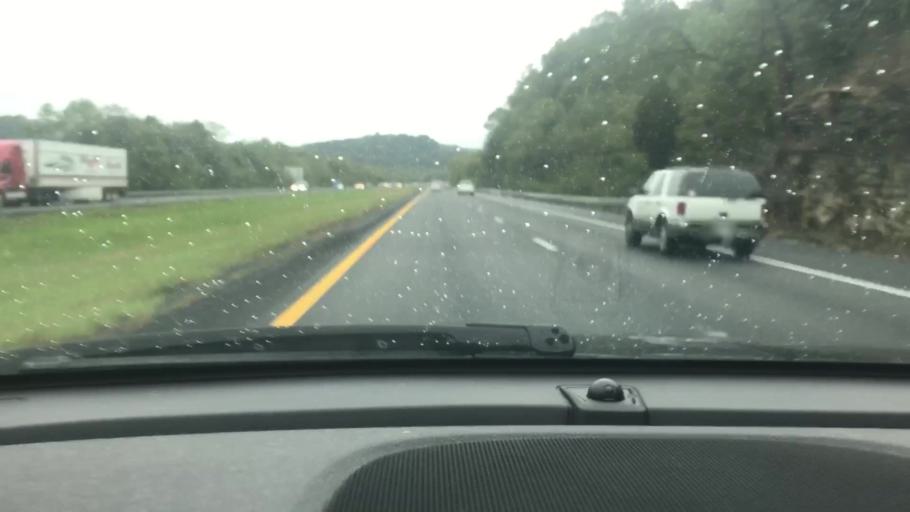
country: US
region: Tennessee
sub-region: Cheatham County
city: Pegram
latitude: 36.0774
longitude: -87.0017
